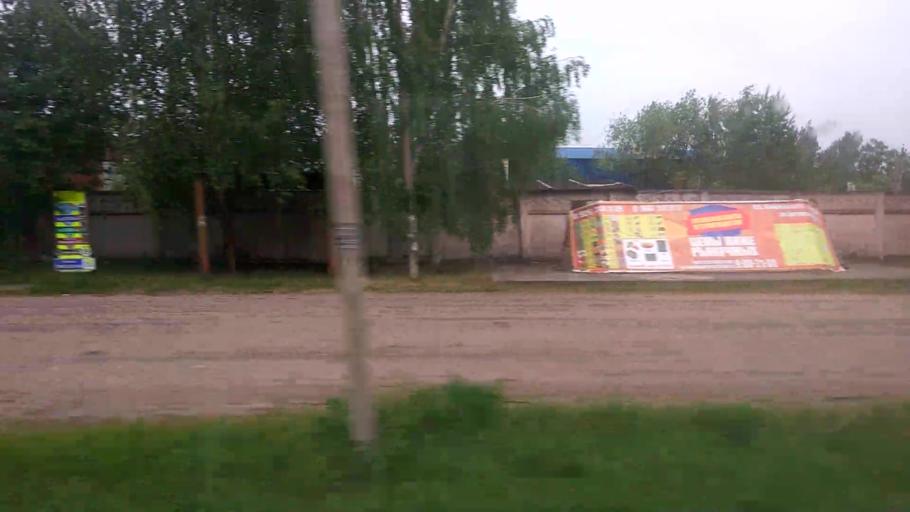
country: RU
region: Moskovskaya
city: Lukhovitsy
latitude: 54.9244
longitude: 38.9957
